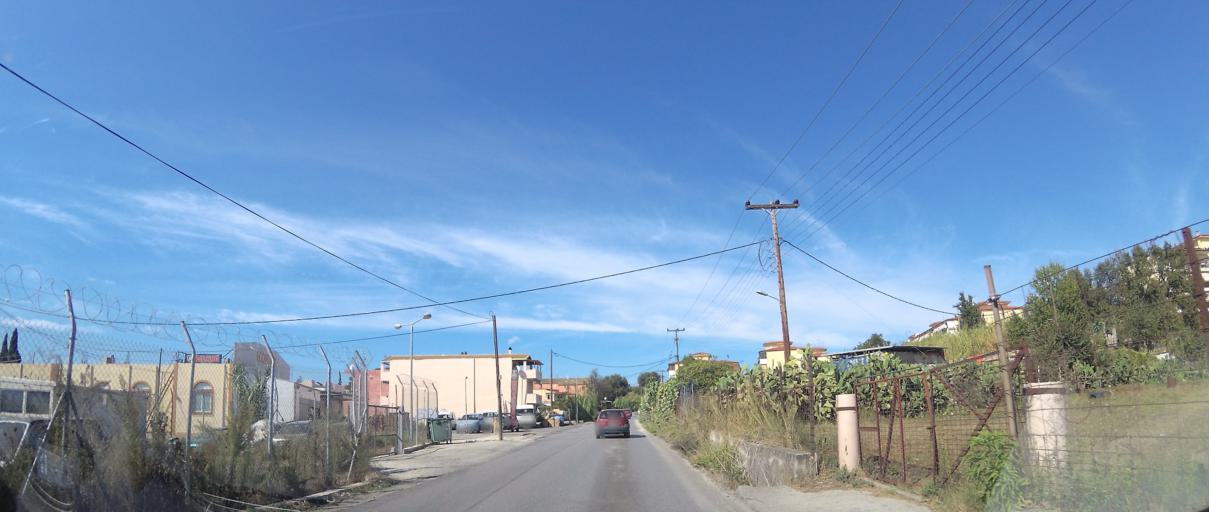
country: GR
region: Ionian Islands
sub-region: Nomos Kerkyras
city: Alepou
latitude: 39.6130
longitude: 19.9037
